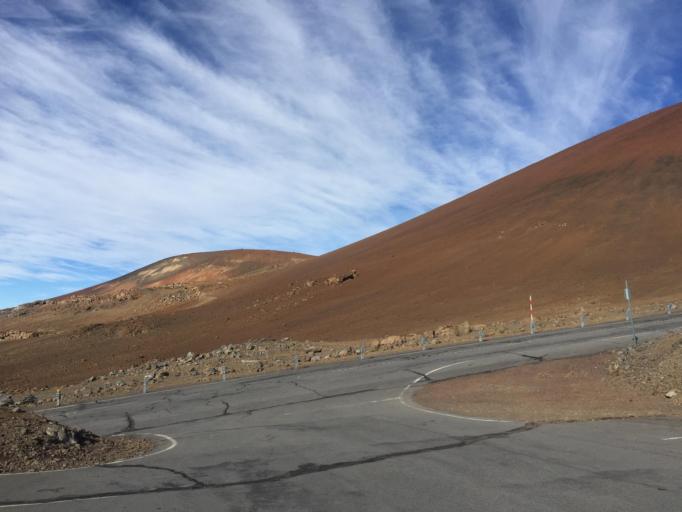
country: US
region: Hawaii
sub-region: Hawaii County
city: Honoka'a
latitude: 19.8104
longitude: -155.4677
